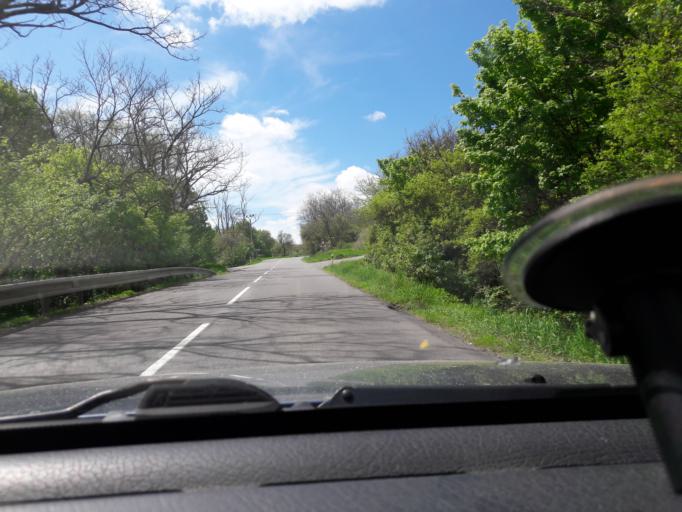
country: SK
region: Banskobystricky
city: Krupina
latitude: 48.2843
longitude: 18.9801
